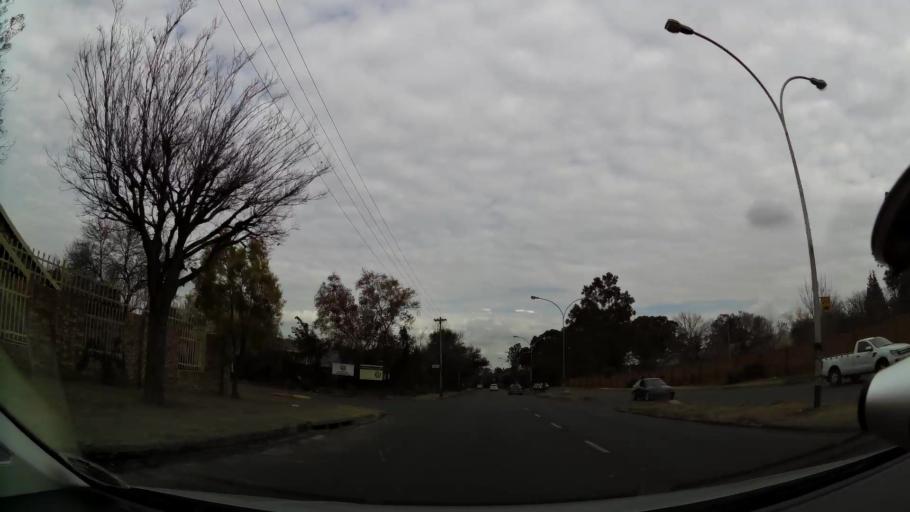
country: ZA
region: Orange Free State
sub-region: Mangaung Metropolitan Municipality
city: Bloemfontein
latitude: -29.0915
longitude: 26.2038
